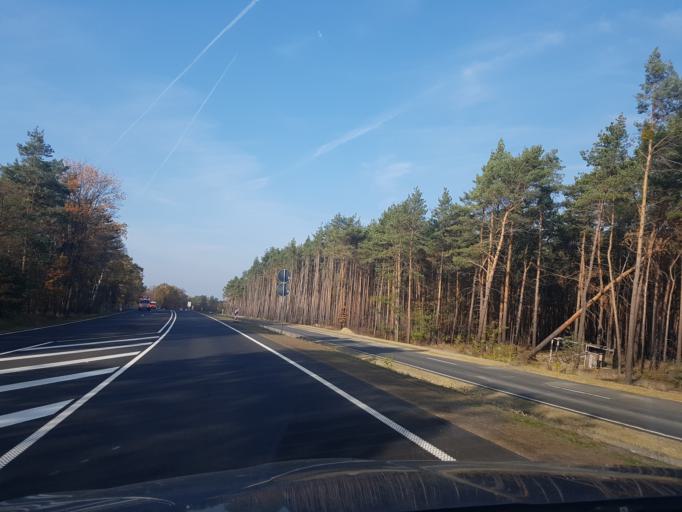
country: DE
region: Brandenburg
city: Elsterwerda
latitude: 51.4872
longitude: 13.4853
